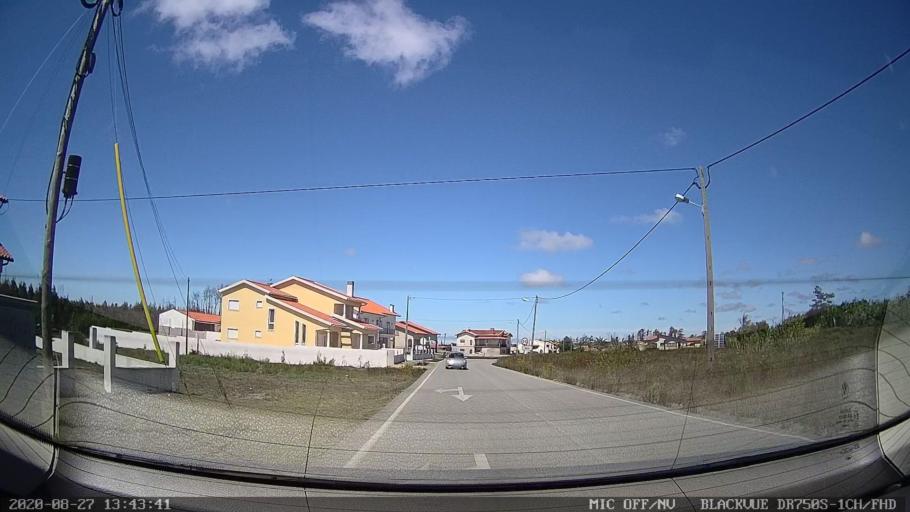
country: PT
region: Coimbra
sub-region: Mira
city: Mira
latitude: 40.4185
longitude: -8.7376
